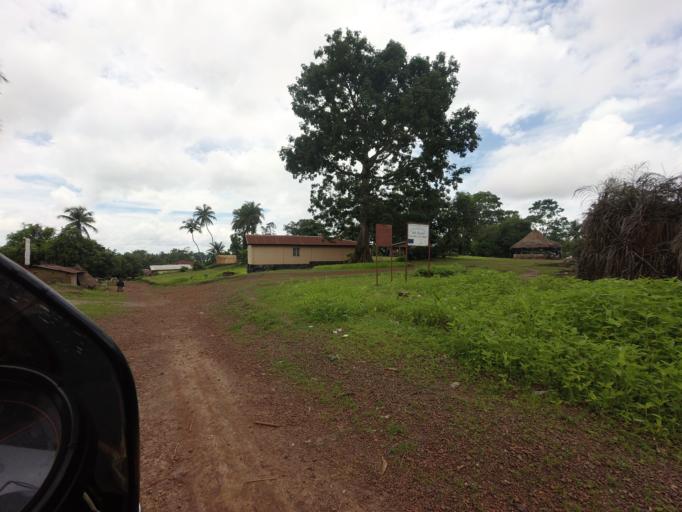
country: SL
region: Northern Province
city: Mambolo
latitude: 8.9722
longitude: -12.9983
